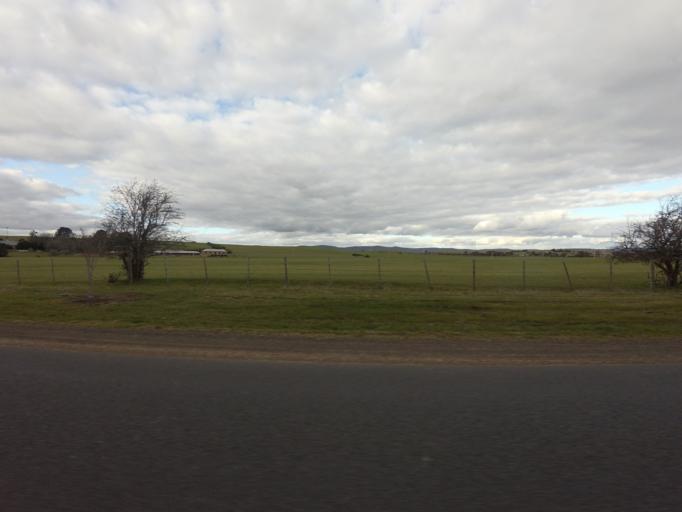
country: AU
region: Tasmania
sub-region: Northern Midlands
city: Evandale
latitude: -42.0211
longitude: 147.4924
